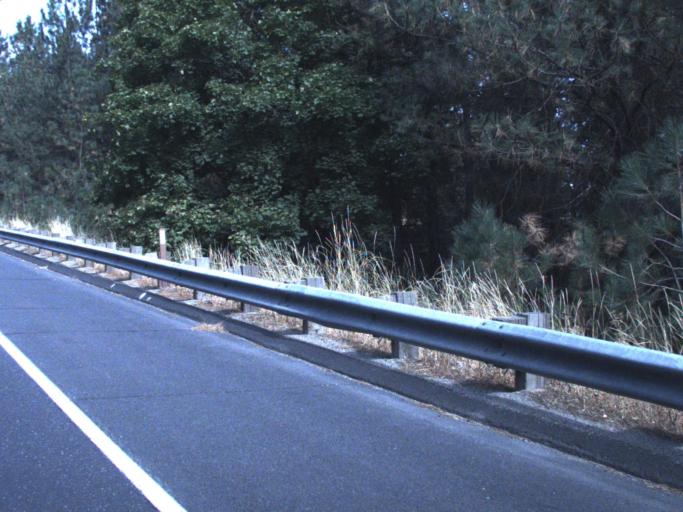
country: US
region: Washington
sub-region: Spokane County
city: Deer Park
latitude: 47.9252
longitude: -117.4605
